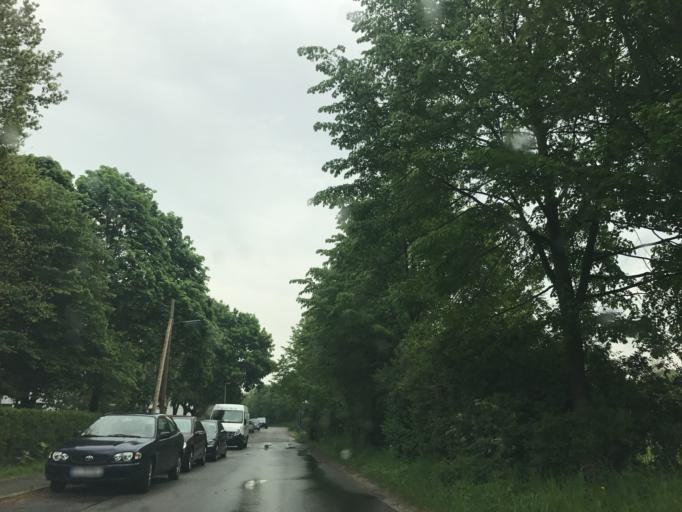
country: DE
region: Berlin
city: Staaken
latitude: 52.5470
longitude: 13.1512
